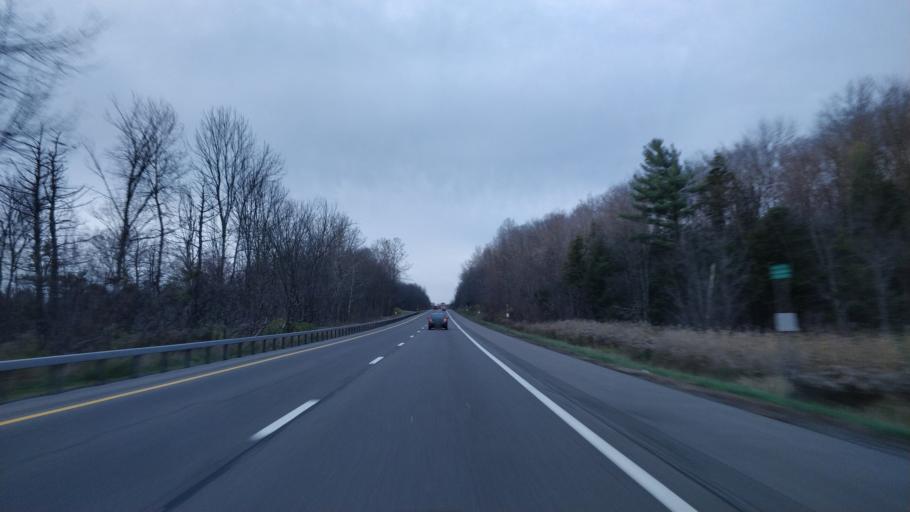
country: US
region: New York
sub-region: Oswego County
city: Central Square
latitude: 43.3530
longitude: -76.1215
